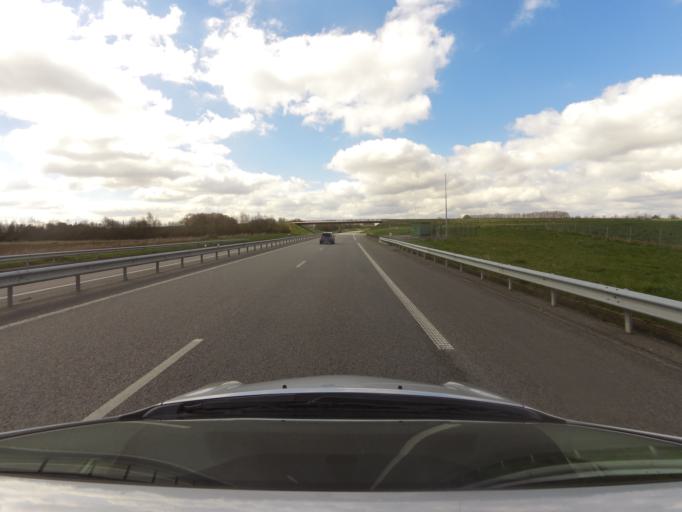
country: FR
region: Haute-Normandie
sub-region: Departement de la Seine-Maritime
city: Yerville
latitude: 49.6582
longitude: 0.9035
